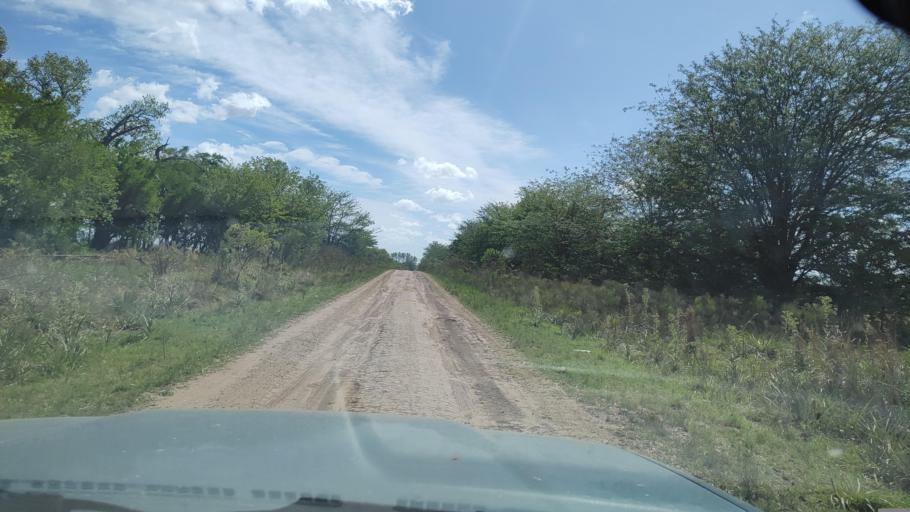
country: AR
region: Buenos Aires
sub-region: Partido de Lujan
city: Lujan
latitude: -34.5193
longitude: -59.1651
